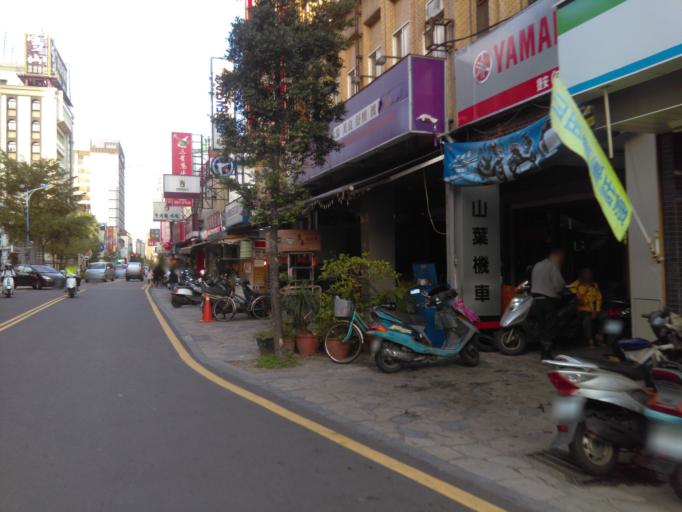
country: TW
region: Taiwan
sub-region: Yilan
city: Yilan
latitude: 24.8266
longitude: 121.7735
